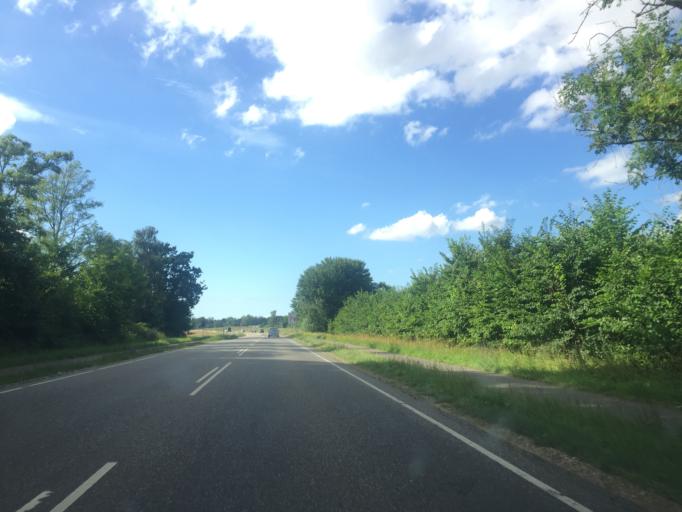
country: DK
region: Zealand
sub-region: Guldborgsund Kommune
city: Nykobing Falster
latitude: 54.7429
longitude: 11.9172
